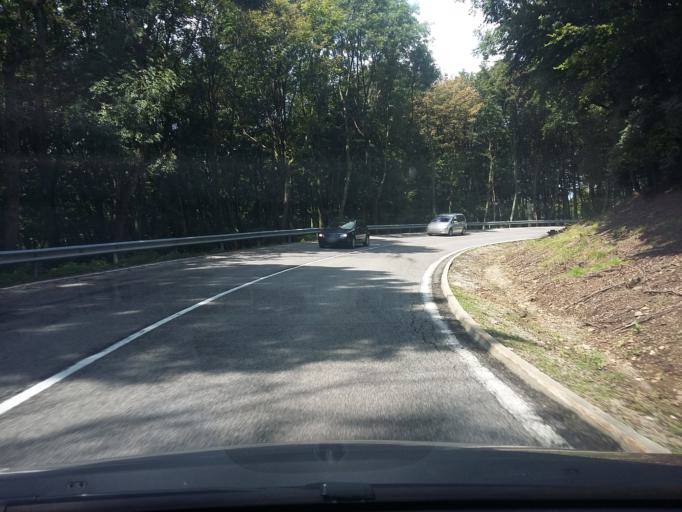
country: SK
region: Bratislavsky
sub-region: Okres Pezinok
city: Pezinok
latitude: 48.3509
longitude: 17.1869
